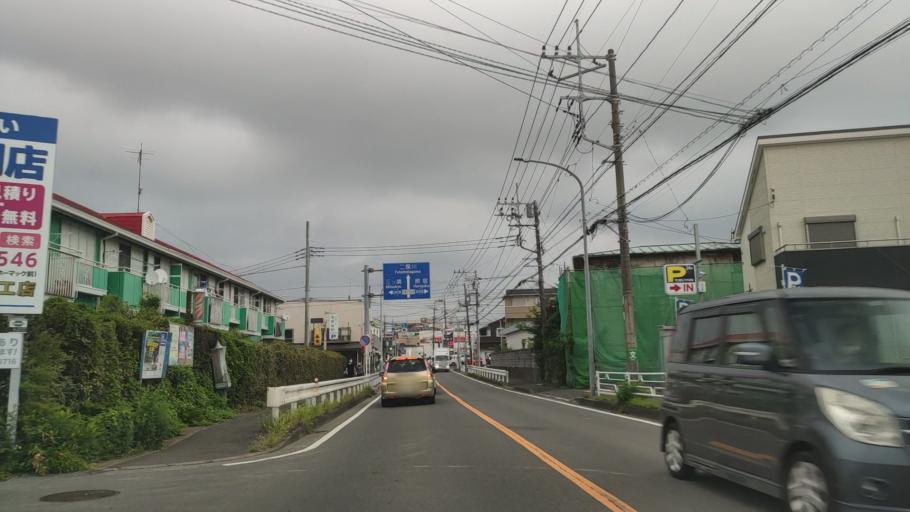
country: JP
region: Kanagawa
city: Minami-rinkan
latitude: 35.4455
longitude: 139.4987
